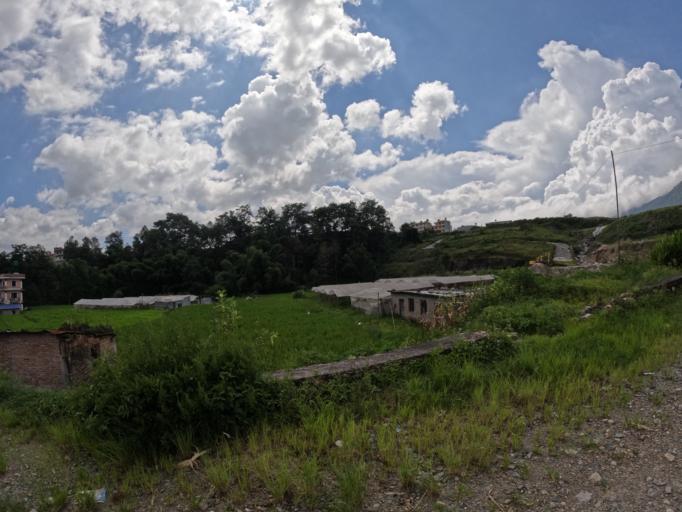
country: NP
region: Central Region
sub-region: Bagmati Zone
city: Kathmandu
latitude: 27.7799
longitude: 85.3277
